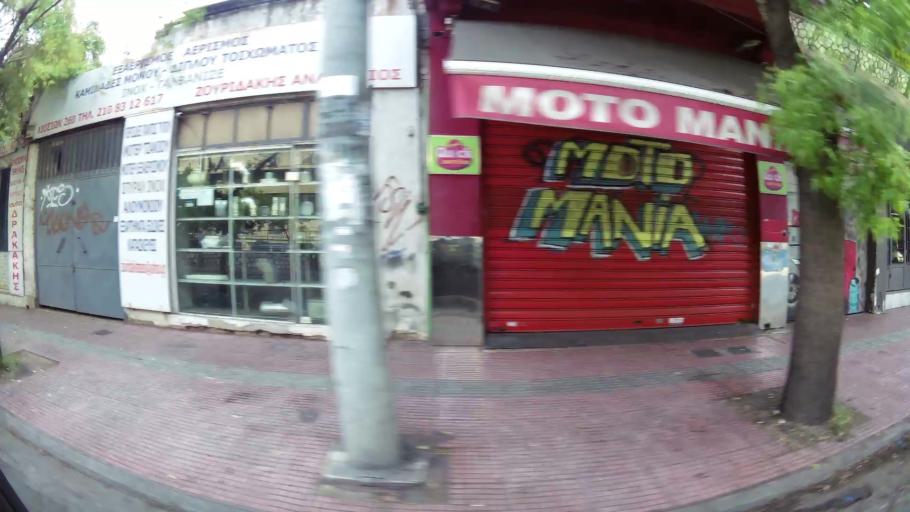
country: GR
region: Attica
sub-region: Nomarchia Athinas
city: Kipseli
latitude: 38.0097
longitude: 23.7213
